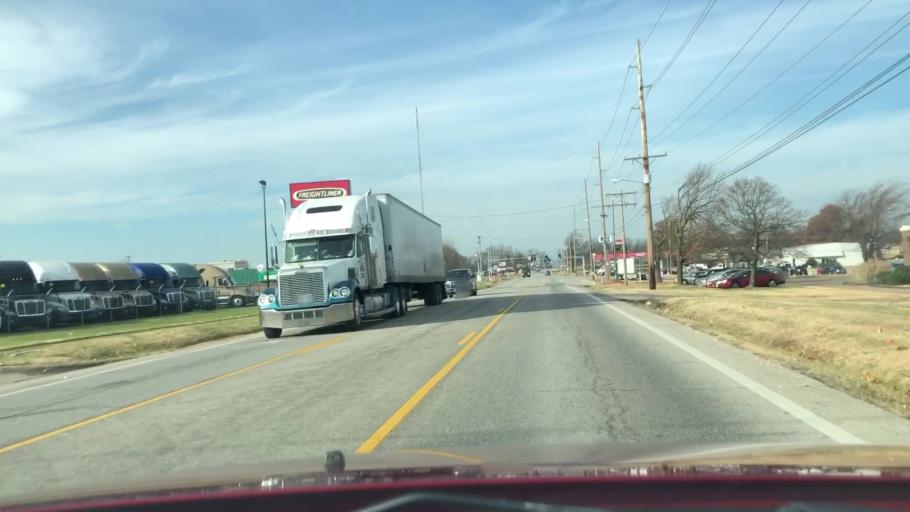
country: US
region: Missouri
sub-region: Greene County
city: Springfield
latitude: 37.2245
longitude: -93.2320
